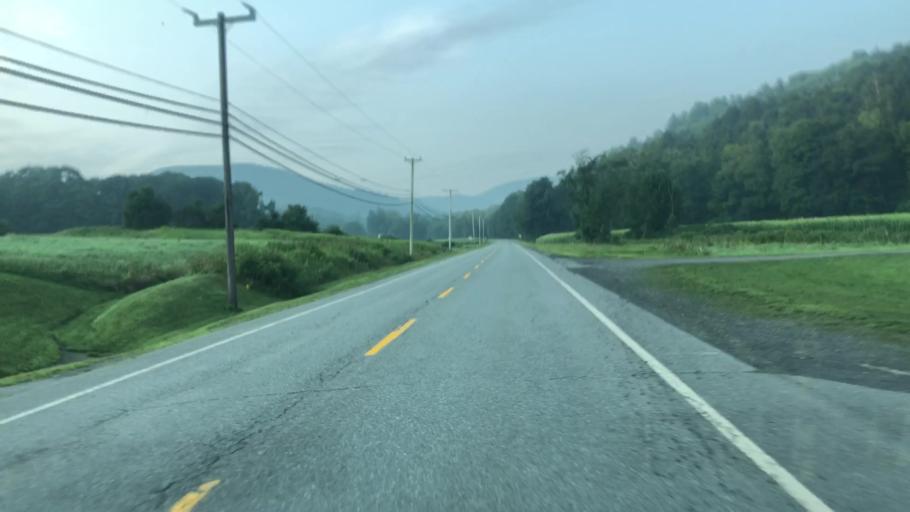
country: US
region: Massachusetts
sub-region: Franklin County
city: Buckland
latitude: 42.5756
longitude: -72.8005
